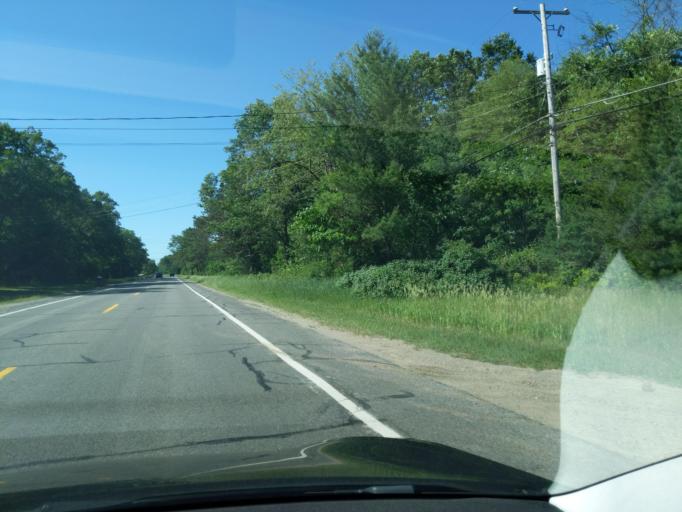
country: US
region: Michigan
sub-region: Muskegon County
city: Lakewood Club
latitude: 43.3657
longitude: -86.2819
